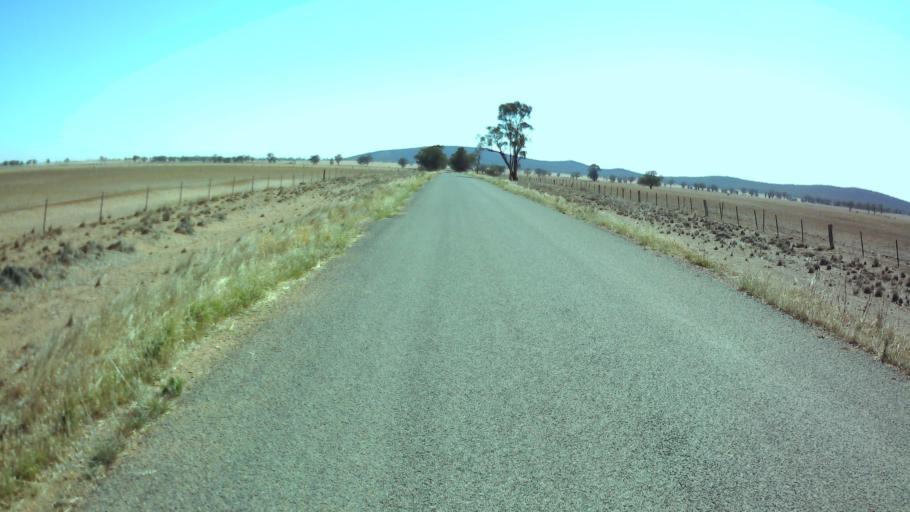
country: AU
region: New South Wales
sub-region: Weddin
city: Grenfell
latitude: -33.7129
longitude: 147.9091
